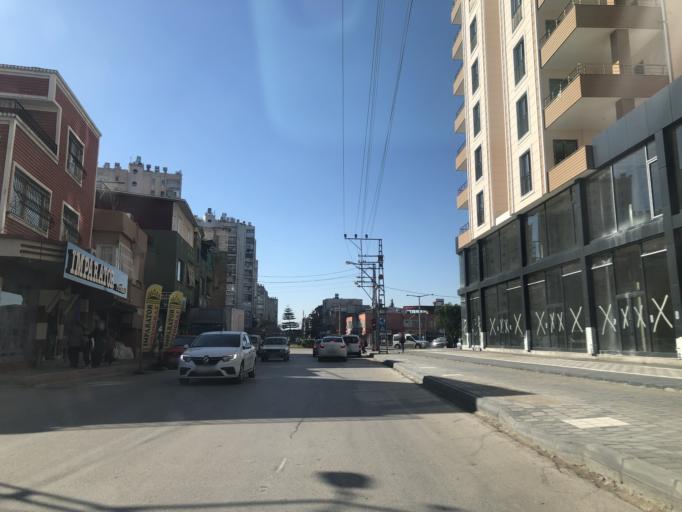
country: TR
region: Adana
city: Yuregir
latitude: 37.0071
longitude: 35.3628
